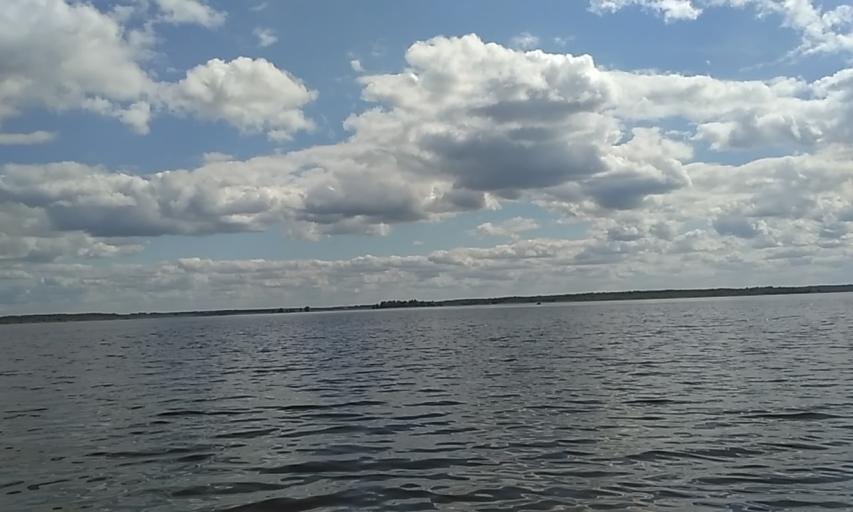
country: BY
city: Novolukoml'
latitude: 54.5909
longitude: 29.1590
